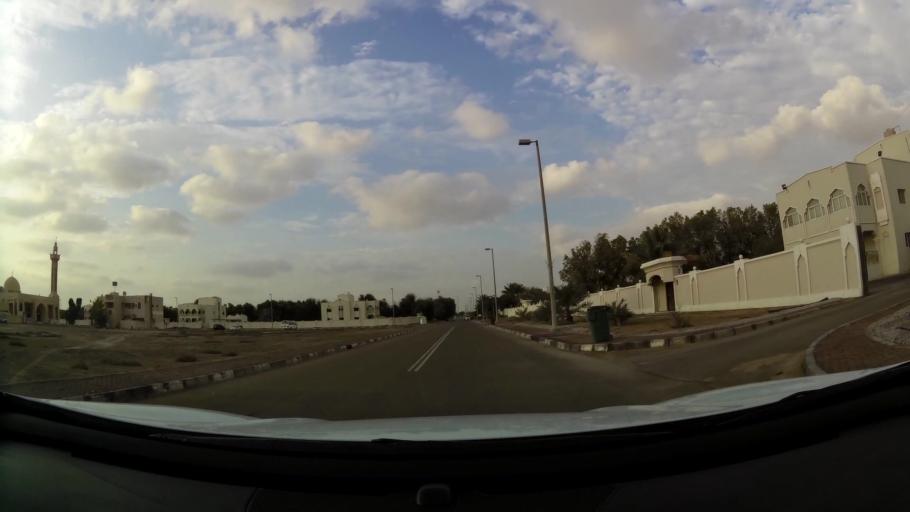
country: AE
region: Abu Dhabi
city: Abu Dhabi
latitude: 24.3808
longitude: 54.5328
